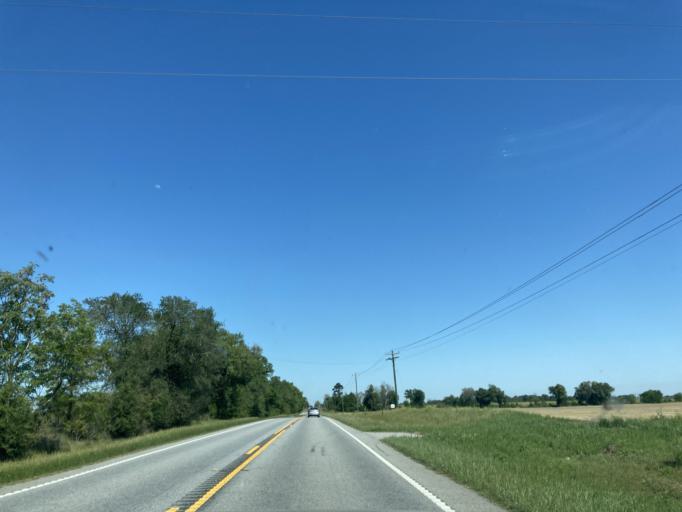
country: US
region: Georgia
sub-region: Miller County
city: Colquitt
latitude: 31.1866
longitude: -84.6470
